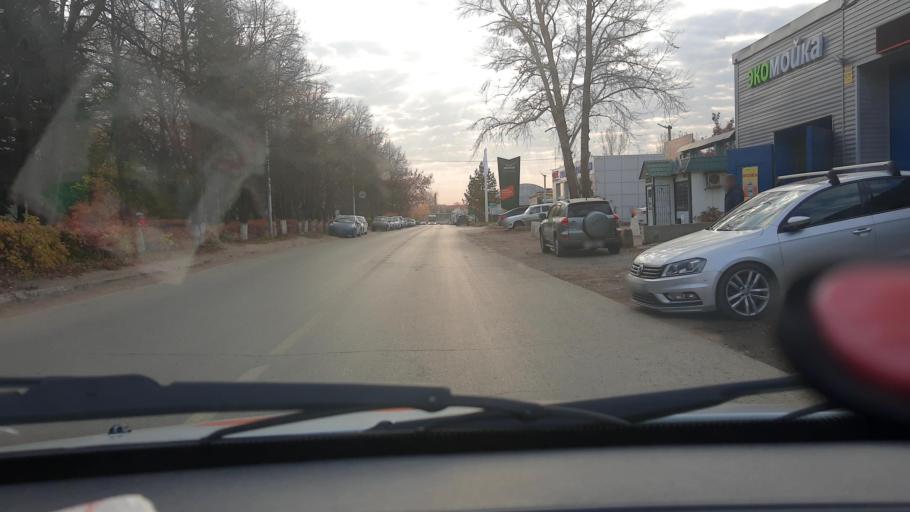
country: RU
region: Bashkortostan
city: Ufa
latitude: 54.8086
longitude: 56.0643
